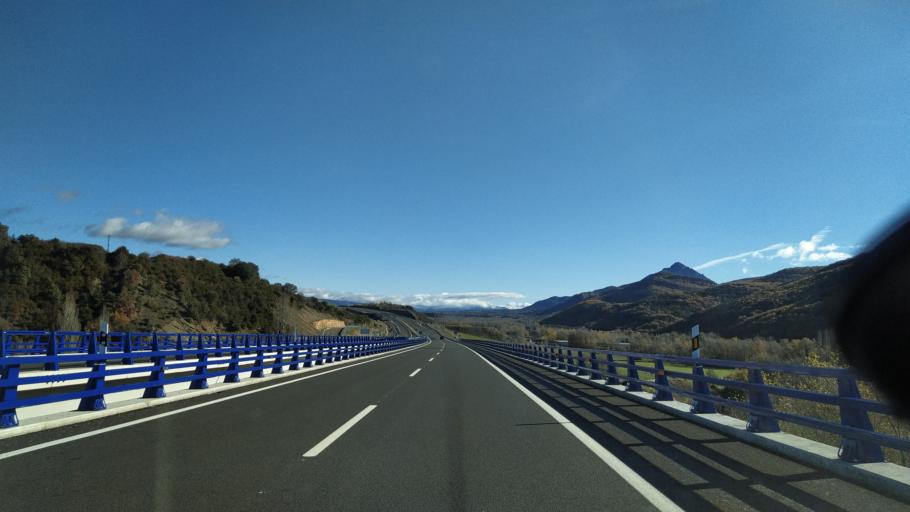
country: ES
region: Aragon
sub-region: Provincia de Huesca
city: Santa Cruz de la Seros
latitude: 42.5616
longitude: -0.6675
